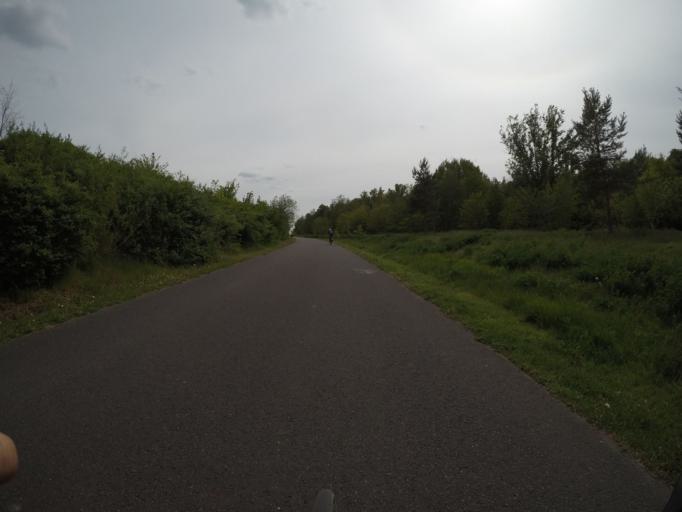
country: DE
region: Berlin
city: Altglienicke
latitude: 52.4205
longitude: 13.5214
